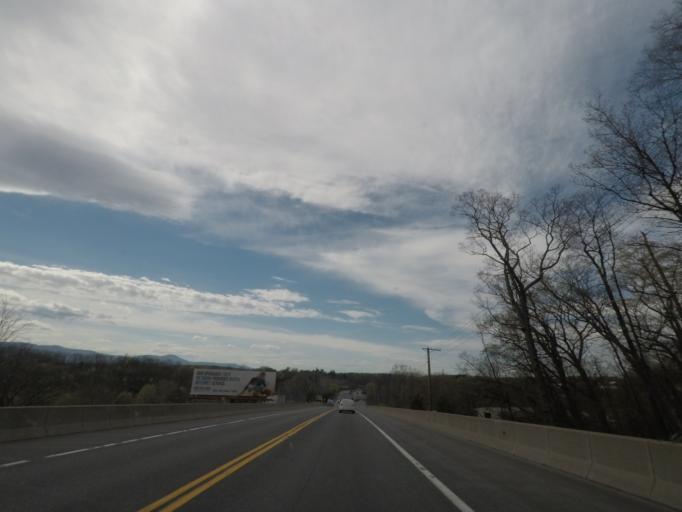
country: US
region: New York
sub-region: Greene County
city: Catskill
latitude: 42.2287
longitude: -73.8652
